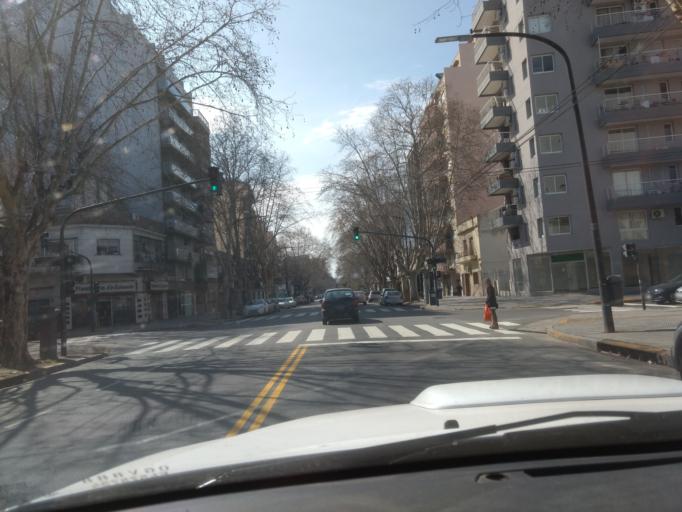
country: AR
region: Buenos Aires F.D.
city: Villa Santa Rita
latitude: -34.5869
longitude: -58.4819
